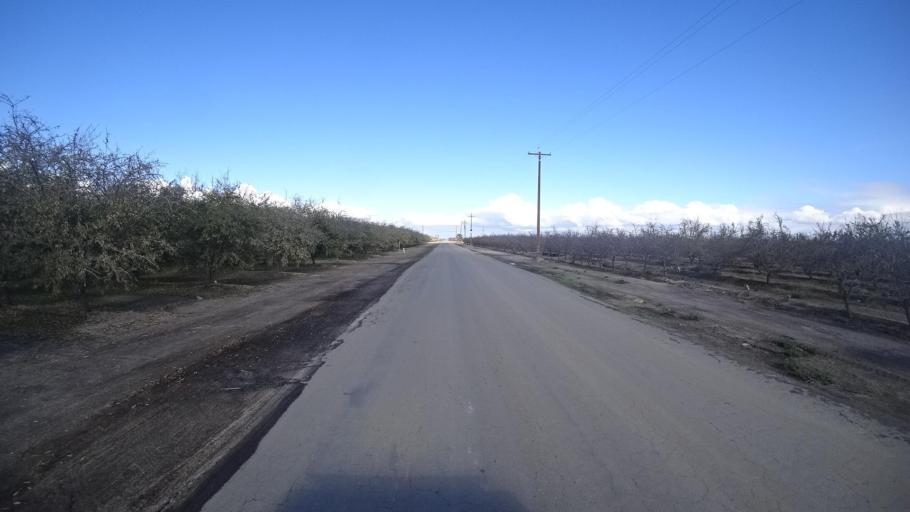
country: US
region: California
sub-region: Kern County
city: Greenacres
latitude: 35.2649
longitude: -119.1284
